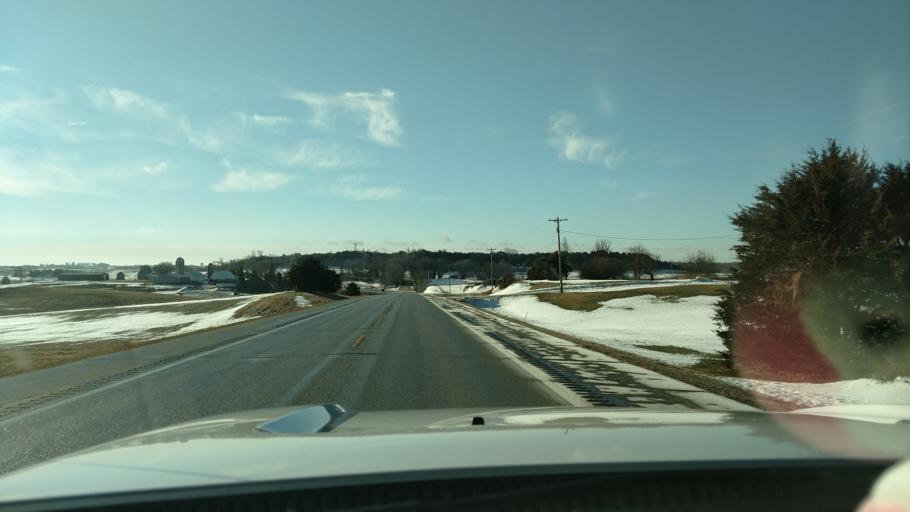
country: US
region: Minnesota
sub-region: Olmsted County
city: Oronoco
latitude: 44.1528
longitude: -92.4194
